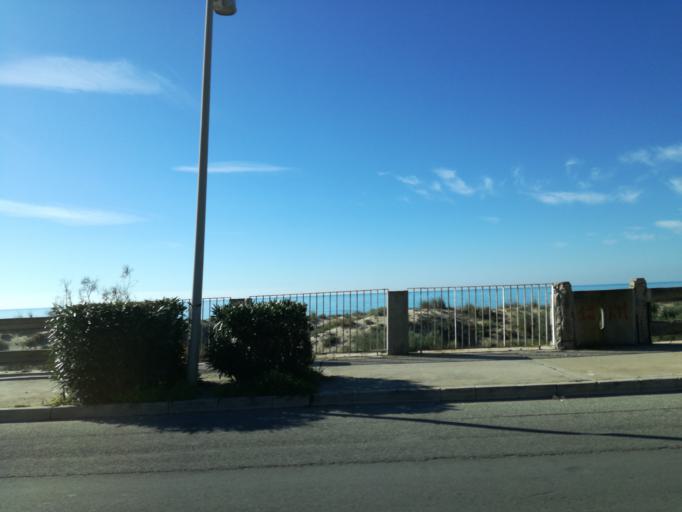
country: IT
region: Sicily
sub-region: Provincia di Caltanissetta
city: Gela
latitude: 37.0704
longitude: 14.2220
